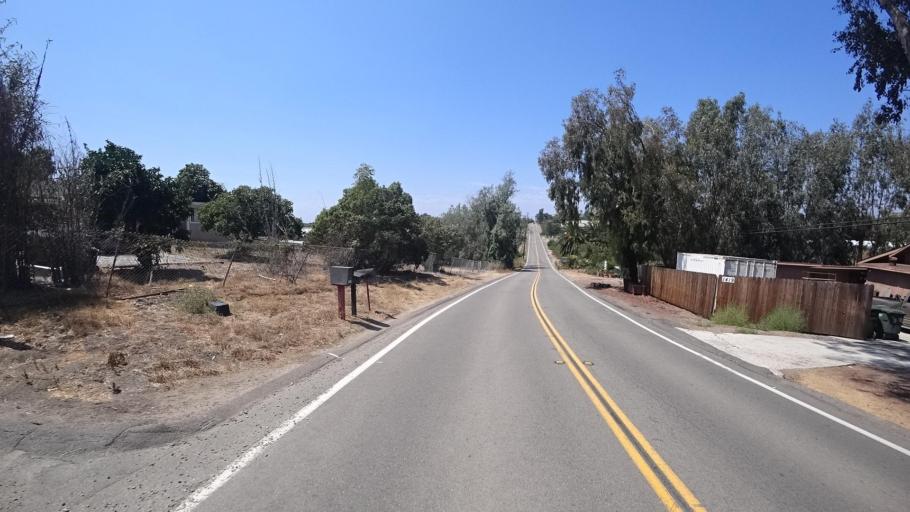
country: US
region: California
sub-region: San Diego County
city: Vista
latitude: 33.1784
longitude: -117.2575
